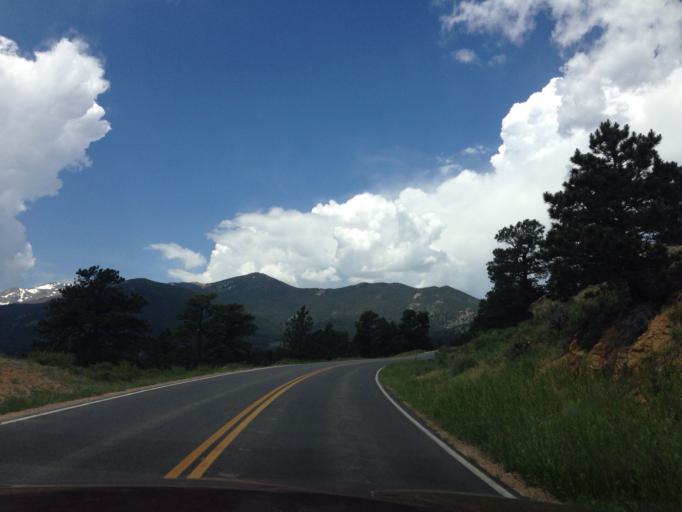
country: US
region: Colorado
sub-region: Larimer County
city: Estes Park
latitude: 40.3710
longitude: -105.5874
